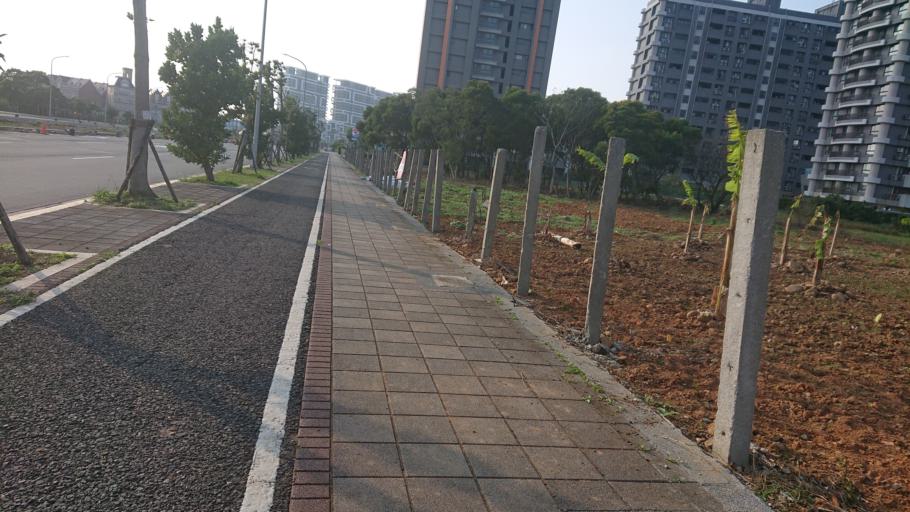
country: TW
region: Taipei
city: Taipei
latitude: 25.1910
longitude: 121.4291
